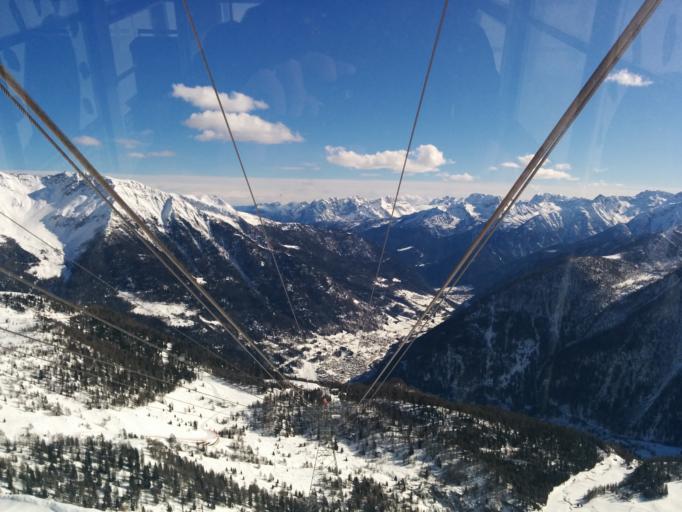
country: IT
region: Trentino-Alto Adige
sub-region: Provincia di Trento
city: Cogolo
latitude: 46.3783
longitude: 10.6420
